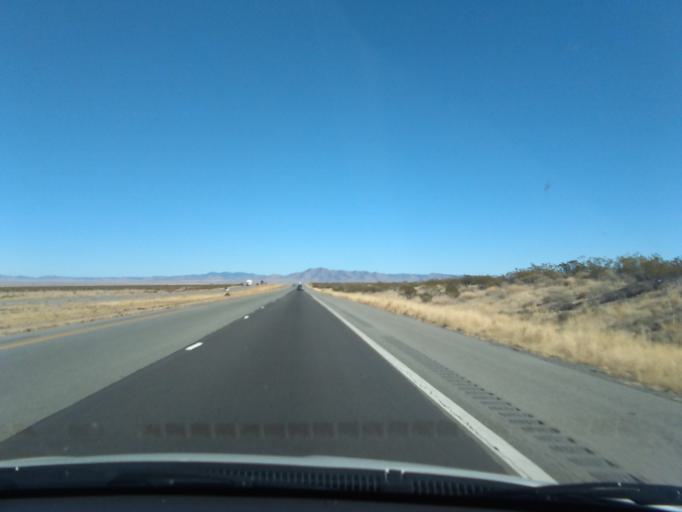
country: US
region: New Mexico
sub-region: Hidalgo County
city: Lordsburg
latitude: 32.3375
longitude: -108.7804
